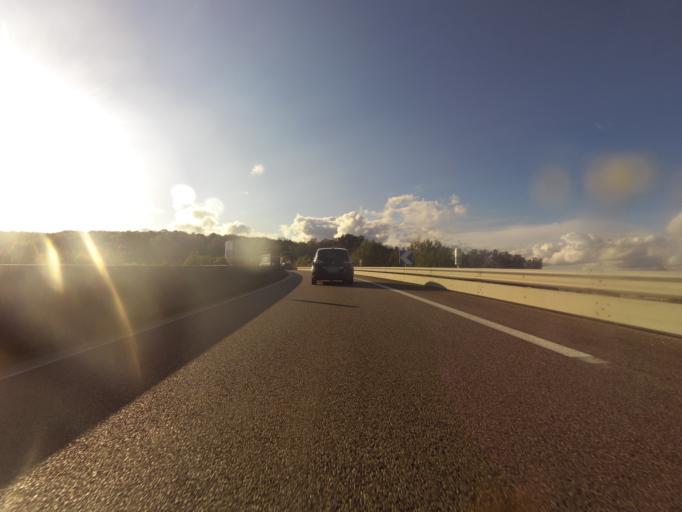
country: FR
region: Haute-Normandie
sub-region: Departement de la Seine-Maritime
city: Neufchatel-en-Bray
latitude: 49.7575
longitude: 1.4872
